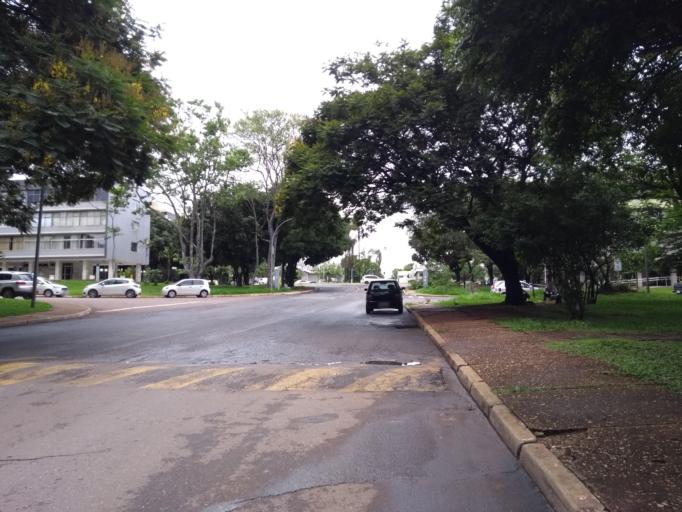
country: BR
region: Federal District
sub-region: Brasilia
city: Brasilia
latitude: -15.7698
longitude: -47.8773
